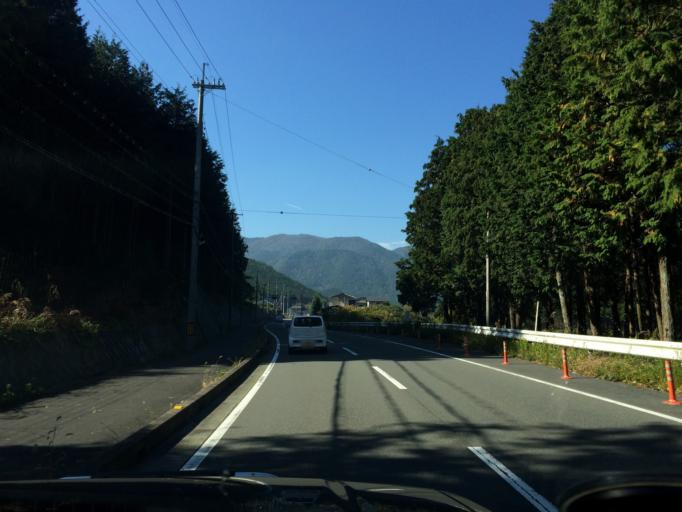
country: JP
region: Kyoto
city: Kameoka
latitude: 35.0490
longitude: 135.4942
